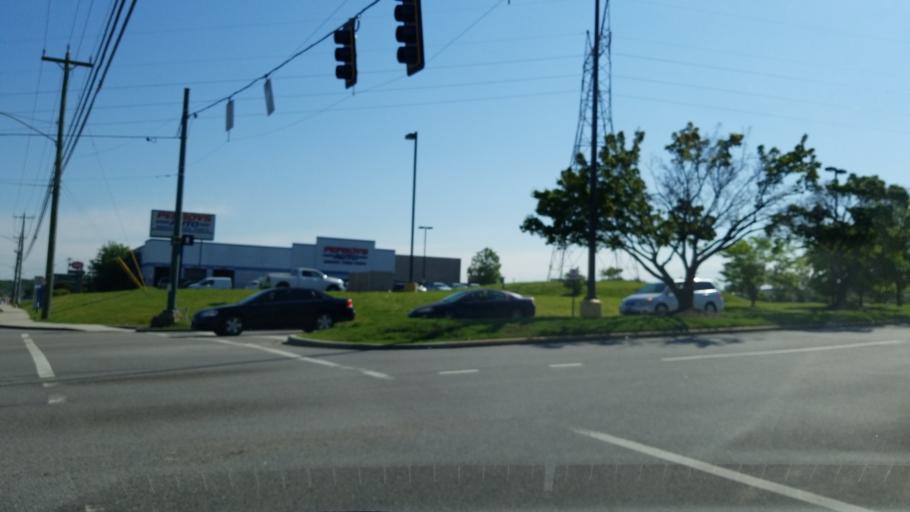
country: US
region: Tennessee
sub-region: Hamilton County
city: East Brainerd
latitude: 35.0321
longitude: -85.1543
